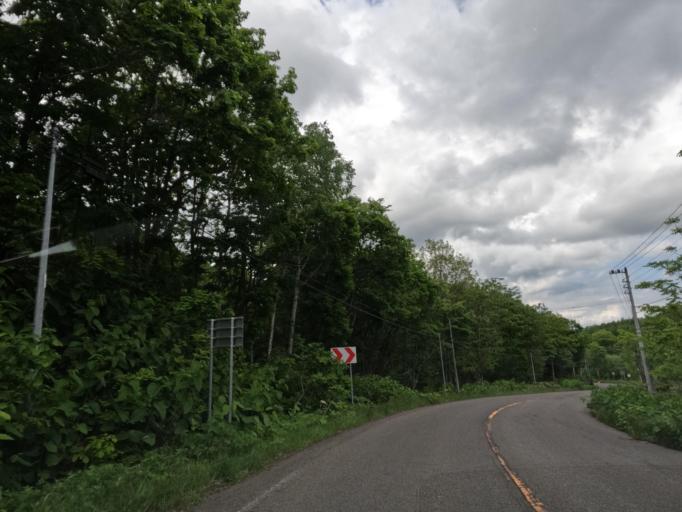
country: JP
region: Hokkaido
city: Takikawa
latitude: 43.5642
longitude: 141.7013
